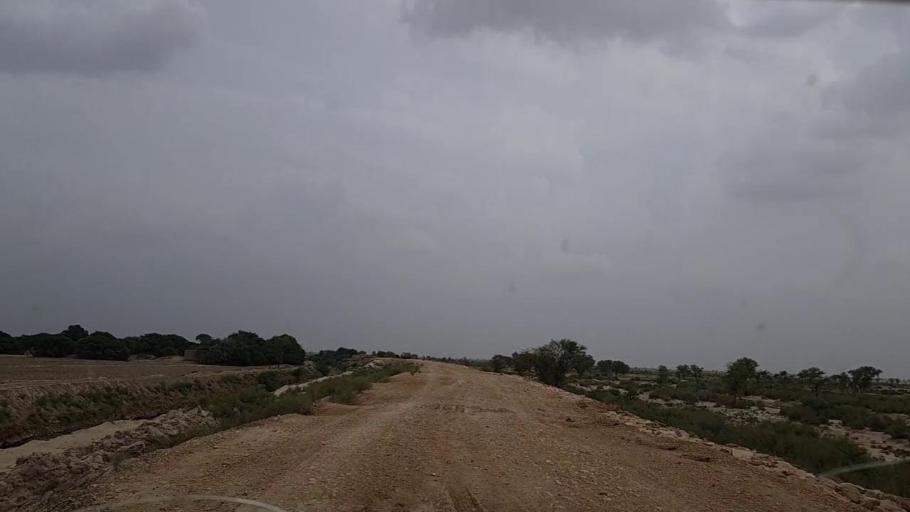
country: PK
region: Sindh
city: Johi
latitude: 26.7232
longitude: 67.5784
